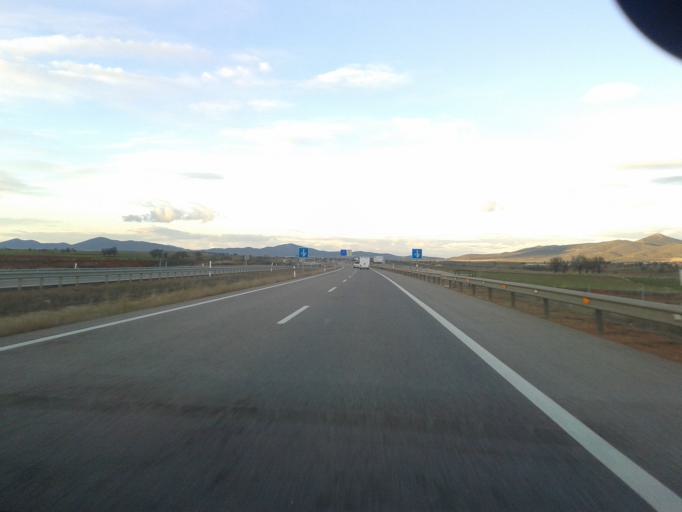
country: ES
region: Aragon
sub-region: Provincia de Zaragoza
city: Romanos
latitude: 41.1099
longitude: -1.2867
